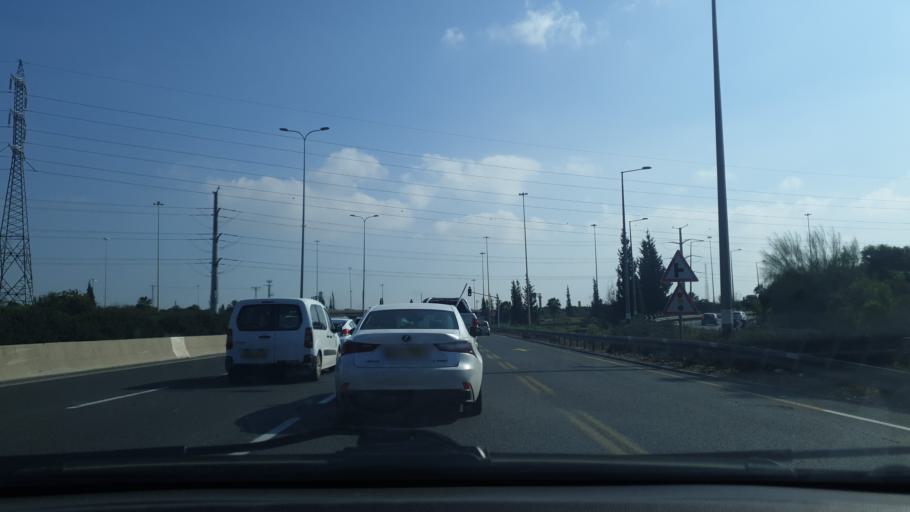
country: IL
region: Tel Aviv
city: Azor
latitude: 32.0129
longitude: 34.8124
